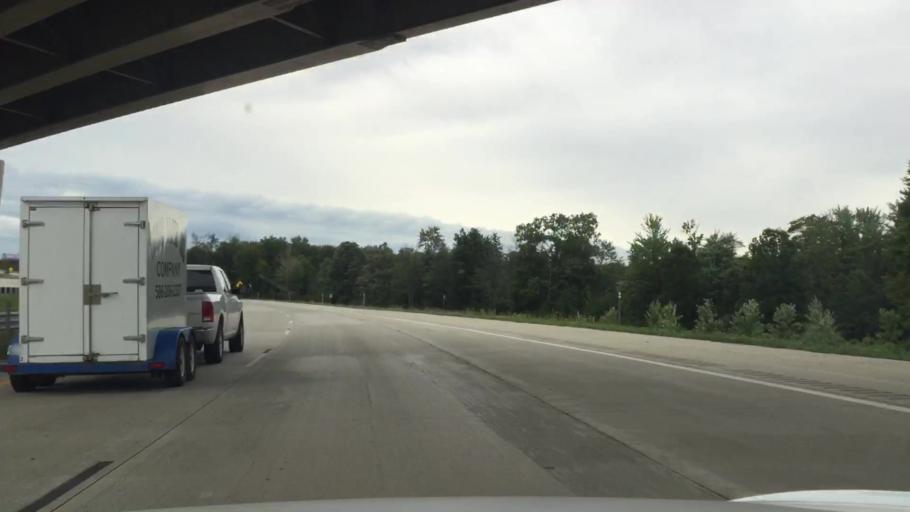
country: US
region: Michigan
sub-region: Saint Clair County
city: Marysville
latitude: 42.9712
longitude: -82.4893
